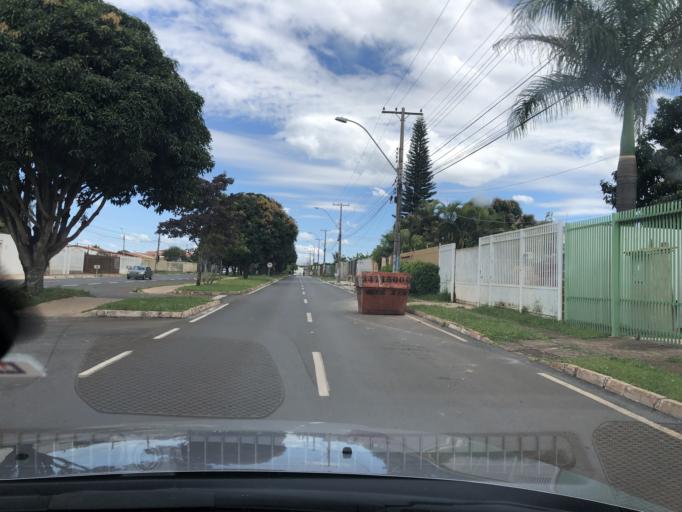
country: BR
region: Federal District
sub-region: Brasilia
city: Brasilia
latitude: -15.9932
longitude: -47.9903
